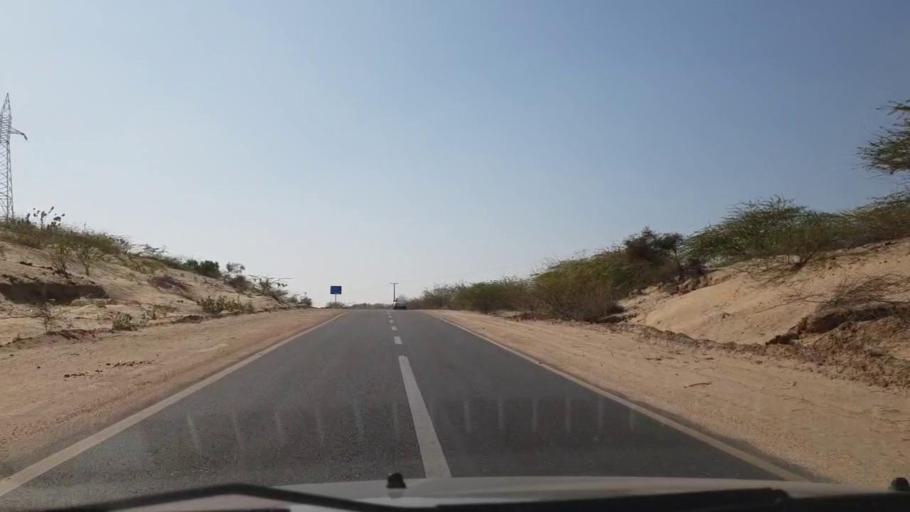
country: PK
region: Sindh
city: Diplo
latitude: 24.4910
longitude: 69.5925
